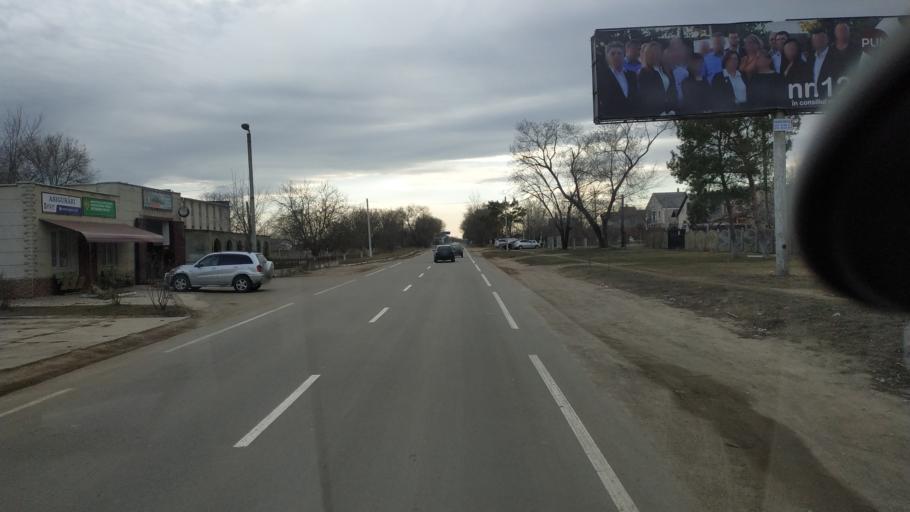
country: MD
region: Criuleni
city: Criuleni
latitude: 47.2029
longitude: 29.1552
